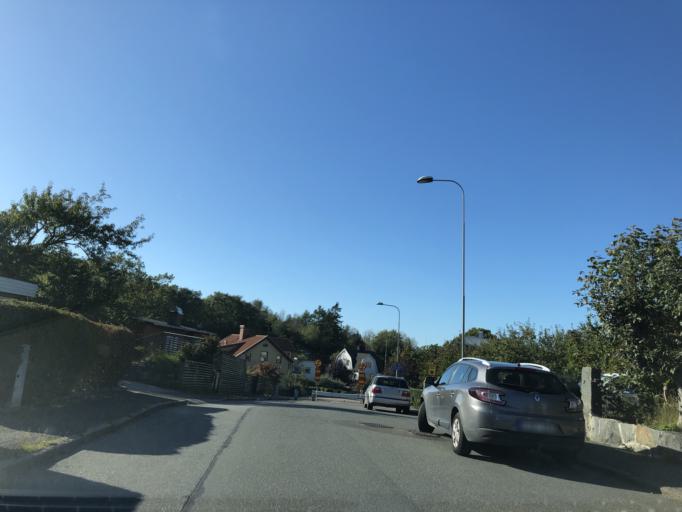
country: SE
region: Vaestra Goetaland
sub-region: Goteborg
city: Majorna
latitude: 57.6617
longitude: 11.8648
